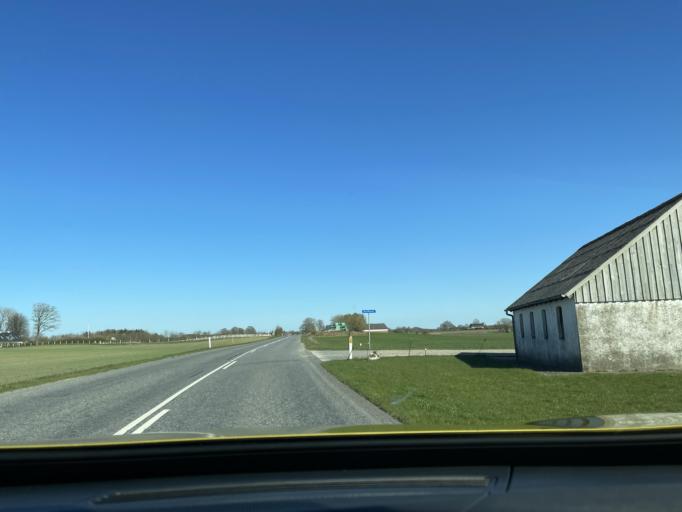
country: DK
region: Central Jutland
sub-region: Silkeborg Kommune
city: Kjellerup
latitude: 56.2593
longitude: 9.3802
